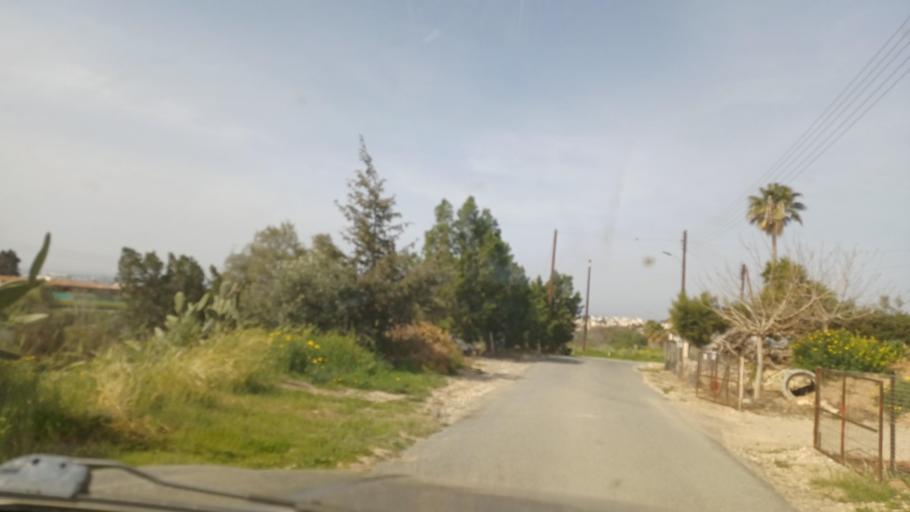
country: CY
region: Pafos
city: Paphos
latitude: 34.7590
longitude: 32.4680
